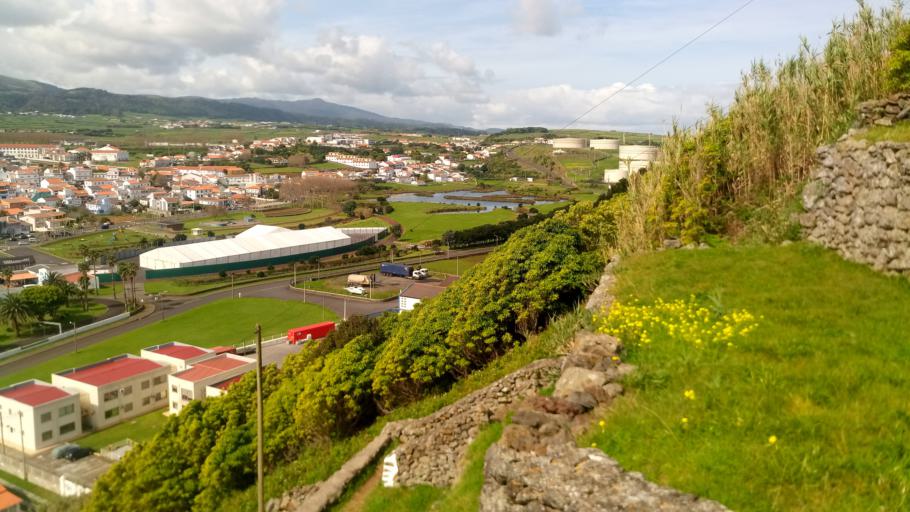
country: PT
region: Azores
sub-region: Praia da Vitoria
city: Praia da Vitoria
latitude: 38.7336
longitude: -27.0547
